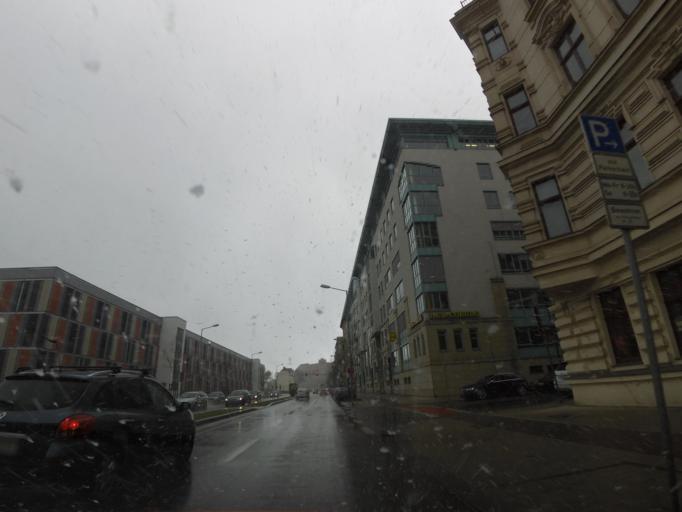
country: DE
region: Saxony-Anhalt
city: Magdeburg
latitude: 52.1205
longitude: 11.6325
